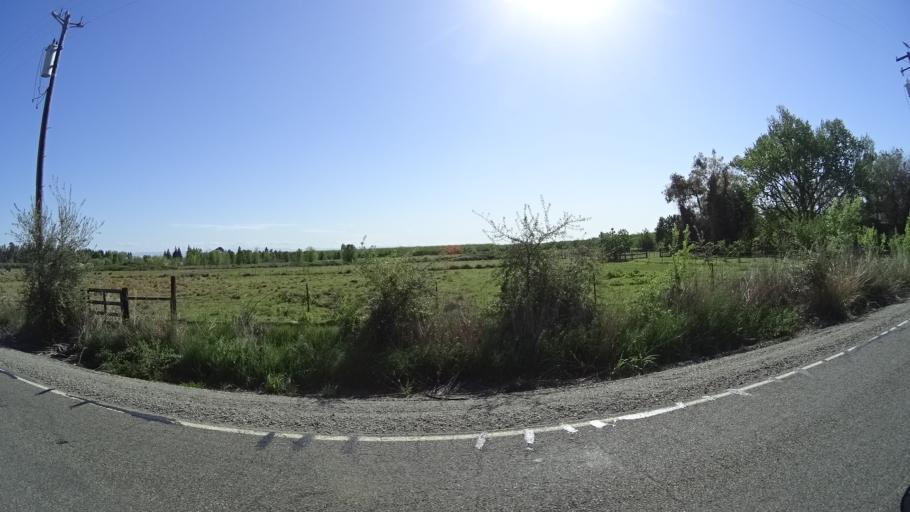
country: US
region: California
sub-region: Glenn County
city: Orland
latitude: 39.7404
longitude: -122.1410
